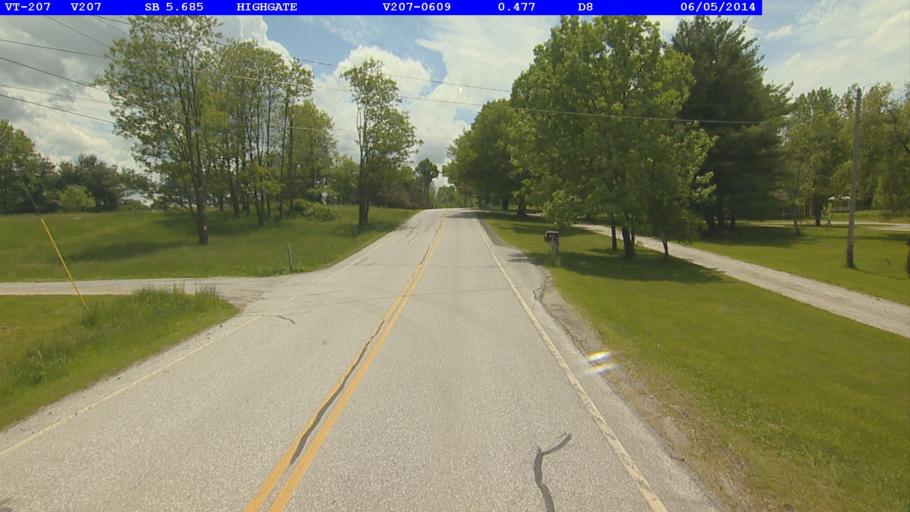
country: US
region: Vermont
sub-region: Franklin County
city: Swanton
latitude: 44.9182
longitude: -73.0556
